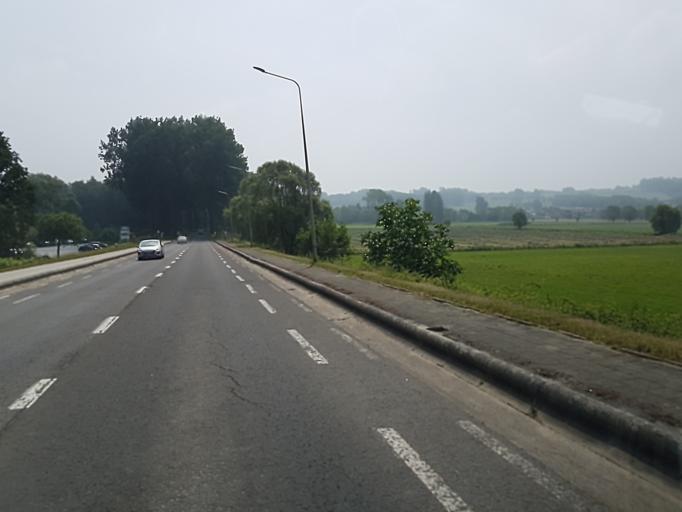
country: BE
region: Flanders
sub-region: Provincie Oost-Vlaanderen
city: Geraardsbergen
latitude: 50.7924
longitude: 3.9023
